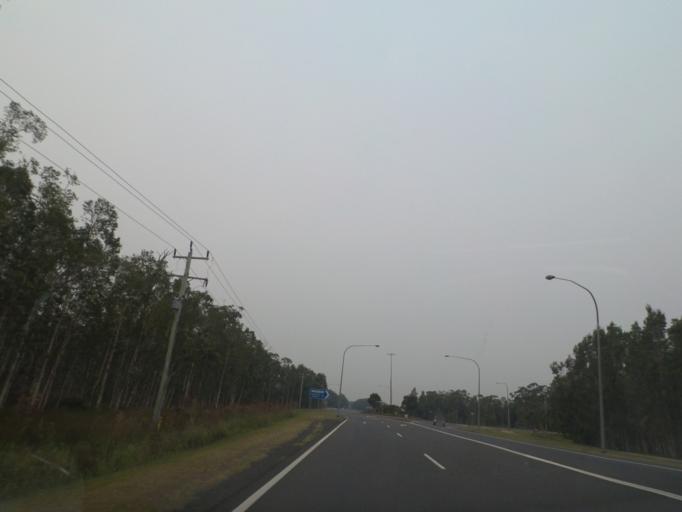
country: AU
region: New South Wales
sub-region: Coffs Harbour
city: Coffs Harbour
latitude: -30.3179
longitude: 153.1105
